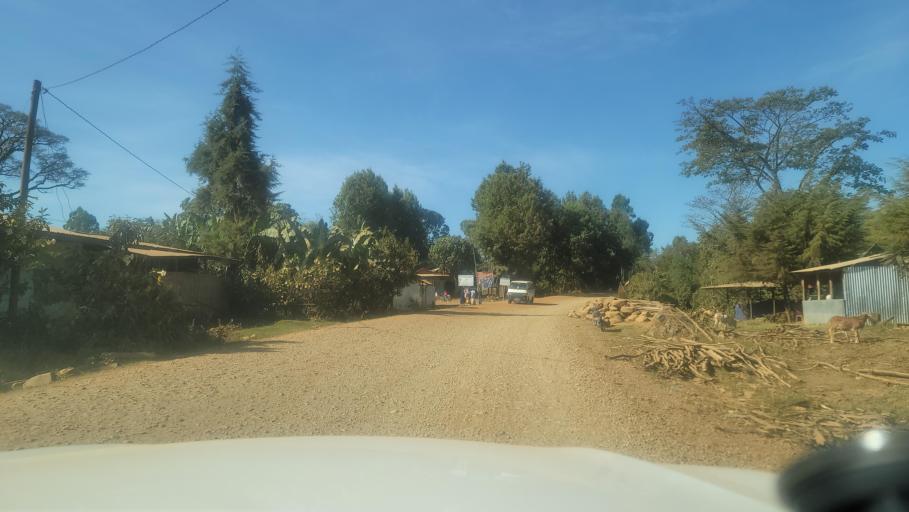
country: ET
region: Oromiya
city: Agaro
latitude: 7.7968
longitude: 36.4948
